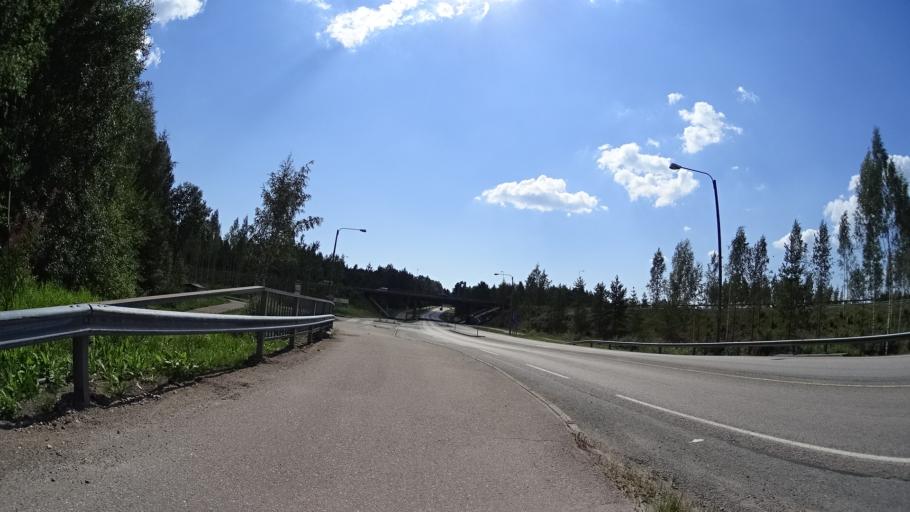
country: FI
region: Uusimaa
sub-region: Helsinki
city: Vantaa
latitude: 60.3243
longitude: 25.0010
